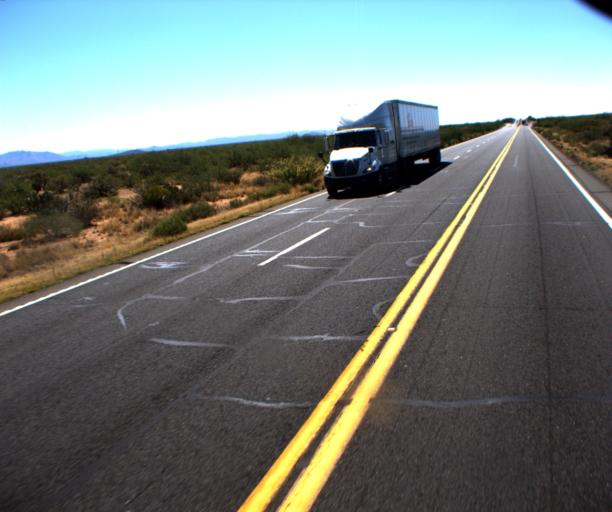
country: US
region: Arizona
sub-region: Yavapai County
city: Congress
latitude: 34.1288
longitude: -112.9583
